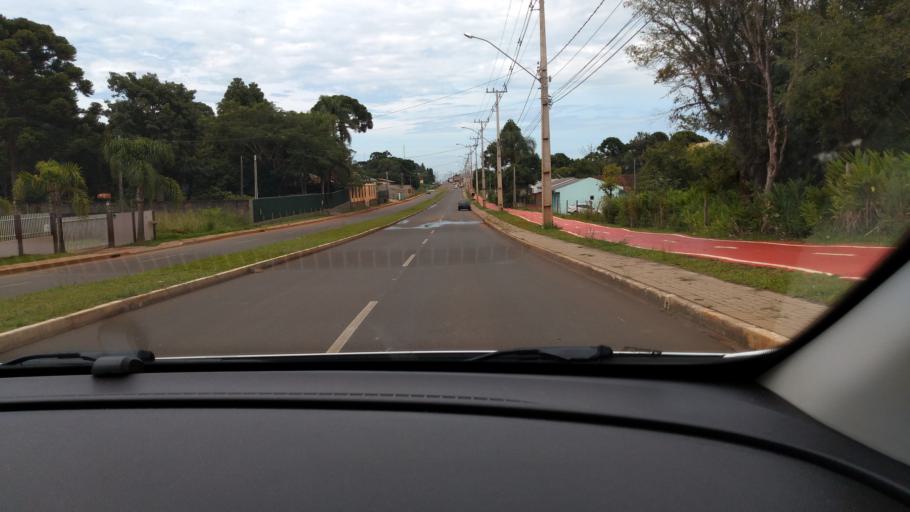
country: BR
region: Parana
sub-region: Guarapuava
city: Guarapuava
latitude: -25.3690
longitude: -51.4385
